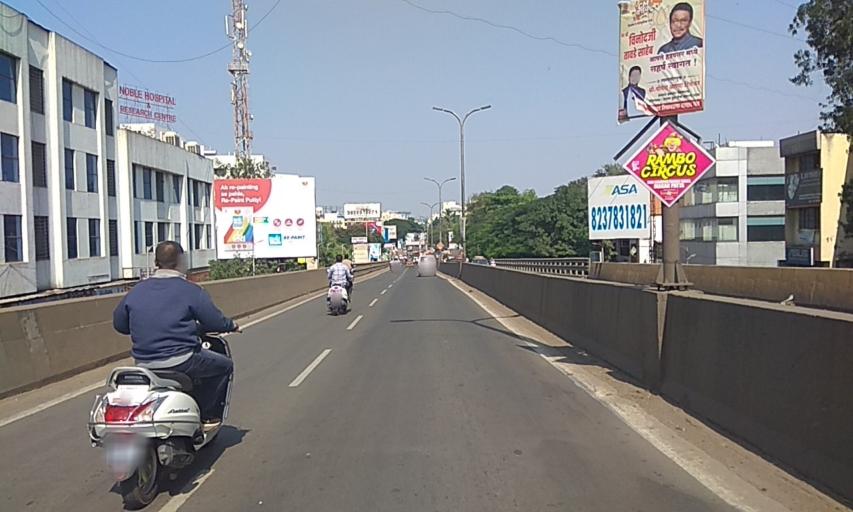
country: IN
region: Maharashtra
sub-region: Pune Division
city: Pune
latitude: 18.5034
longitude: 73.9275
